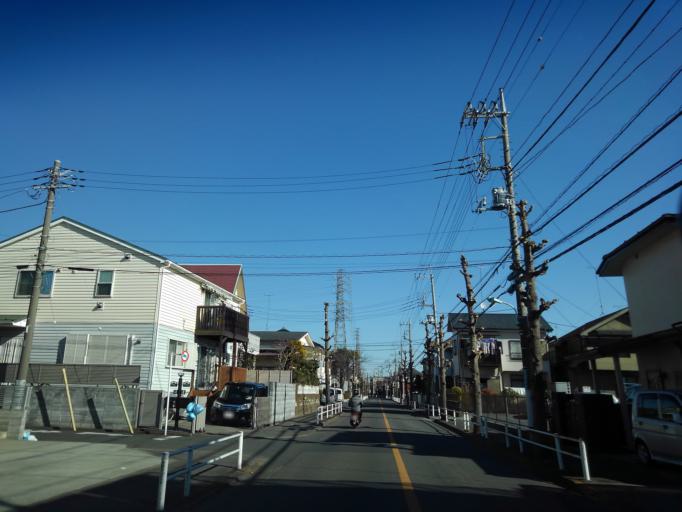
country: JP
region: Tokyo
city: Fussa
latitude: 35.7696
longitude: 139.3125
